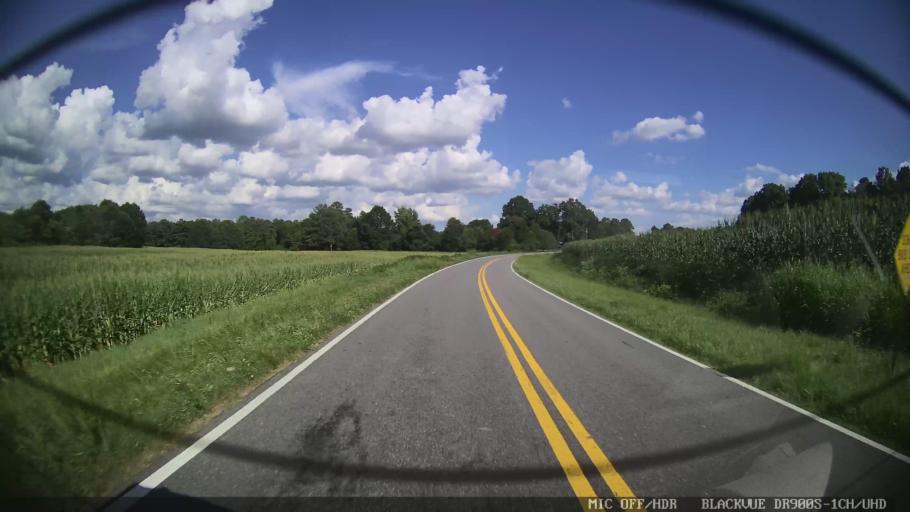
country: US
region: Georgia
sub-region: Bartow County
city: Euharlee
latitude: 34.1529
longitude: -84.9832
